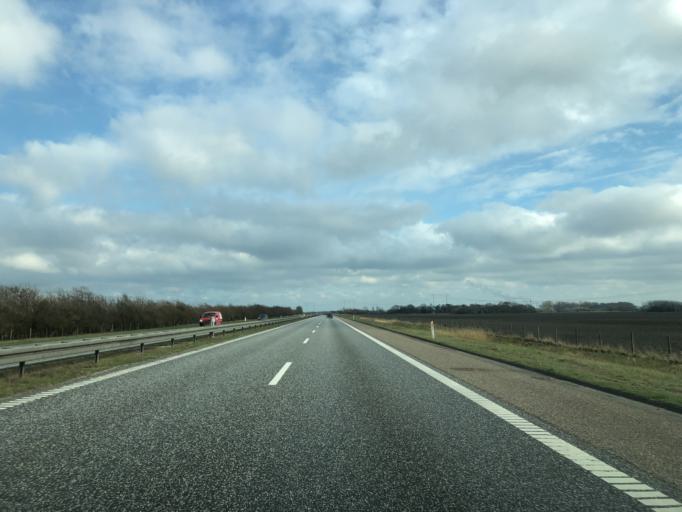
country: DK
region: North Denmark
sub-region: Alborg Kommune
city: Vestbjerg
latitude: 57.1116
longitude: 9.9519
